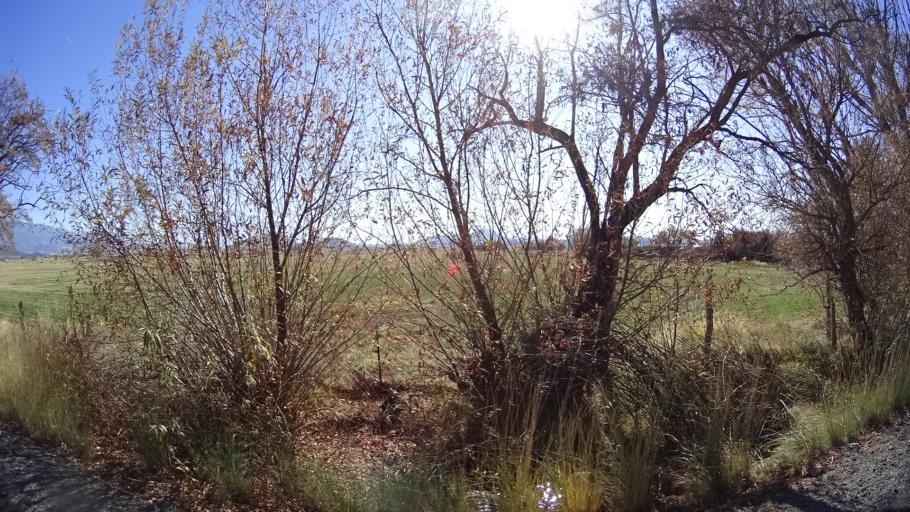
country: US
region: California
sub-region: Siskiyou County
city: Montague
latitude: 41.7263
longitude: -122.4177
